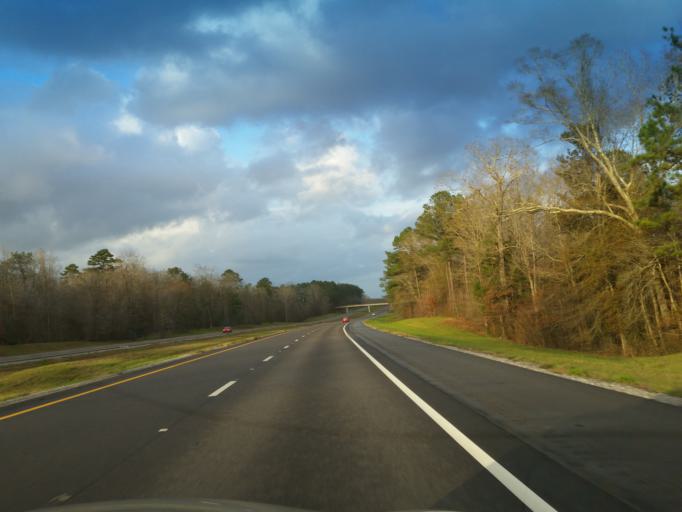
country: US
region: Mississippi
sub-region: Jones County
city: Sharon
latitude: 31.9257
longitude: -89.0017
